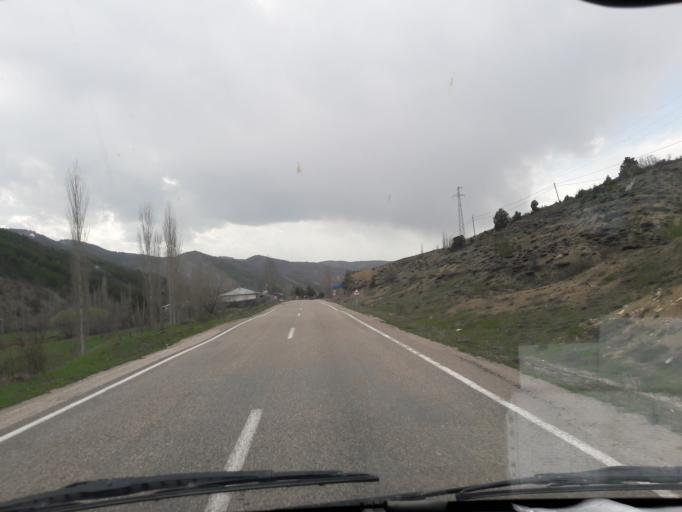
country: TR
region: Giresun
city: Alucra
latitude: 40.2744
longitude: 38.8506
